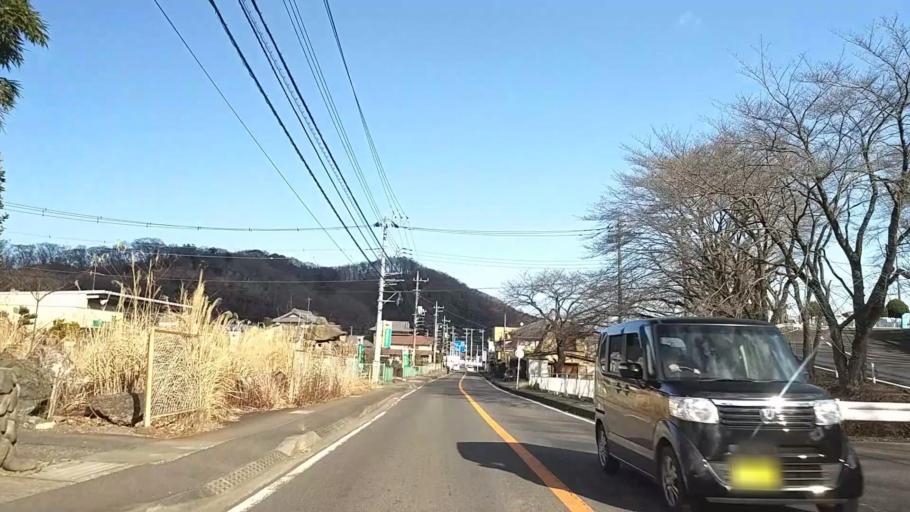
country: JP
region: Kanagawa
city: Isehara
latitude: 35.4329
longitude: 139.3139
